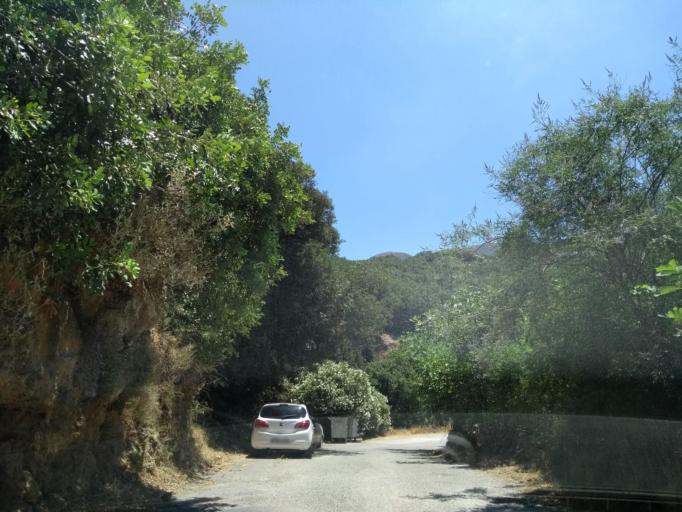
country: GR
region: Crete
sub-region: Nomos Chanias
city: Georgioupolis
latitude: 35.3110
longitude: 24.3089
